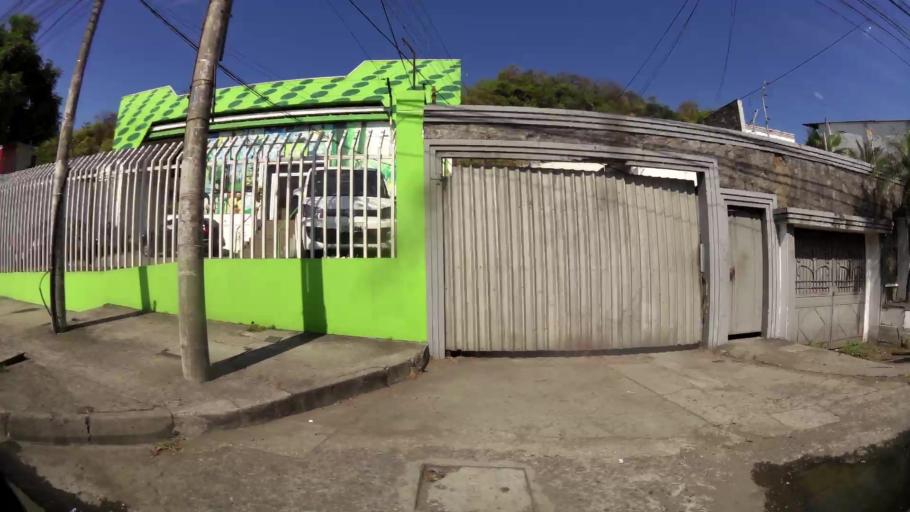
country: EC
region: Guayas
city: Guayaquil
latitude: -2.1770
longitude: -79.9115
